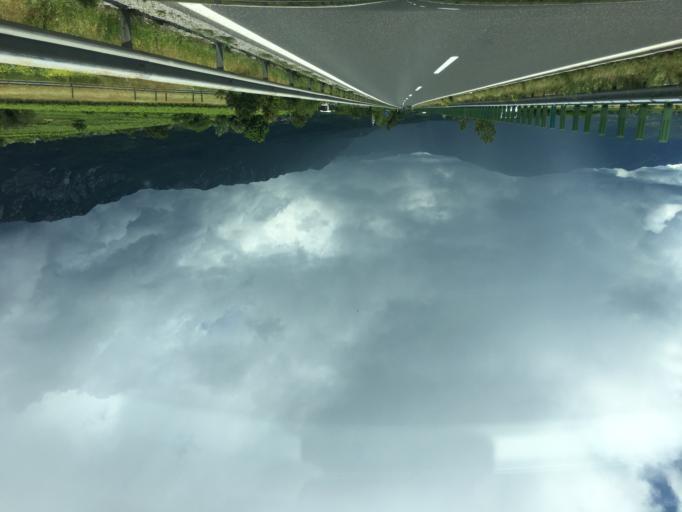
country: SI
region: Vipava
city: Vipava
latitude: 45.8518
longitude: 13.9464
